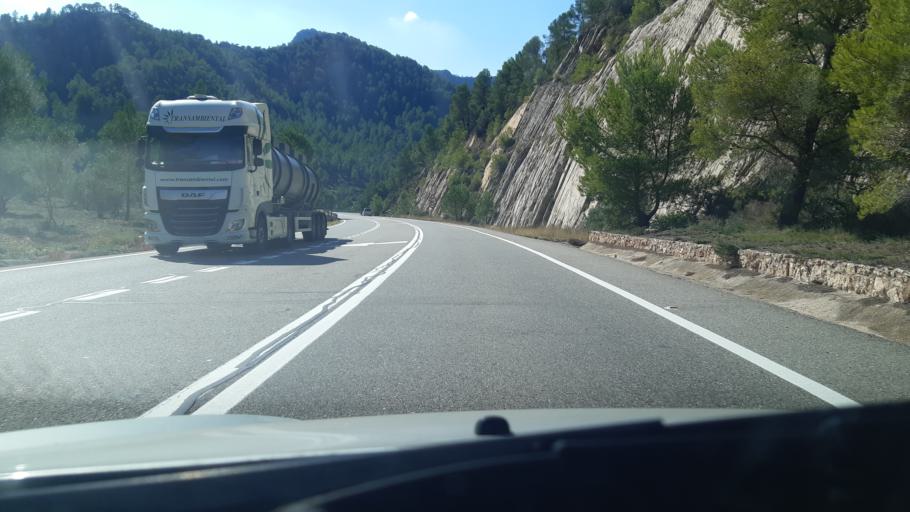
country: ES
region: Catalonia
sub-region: Provincia de Tarragona
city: Rasquera
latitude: 40.9969
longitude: 0.5733
